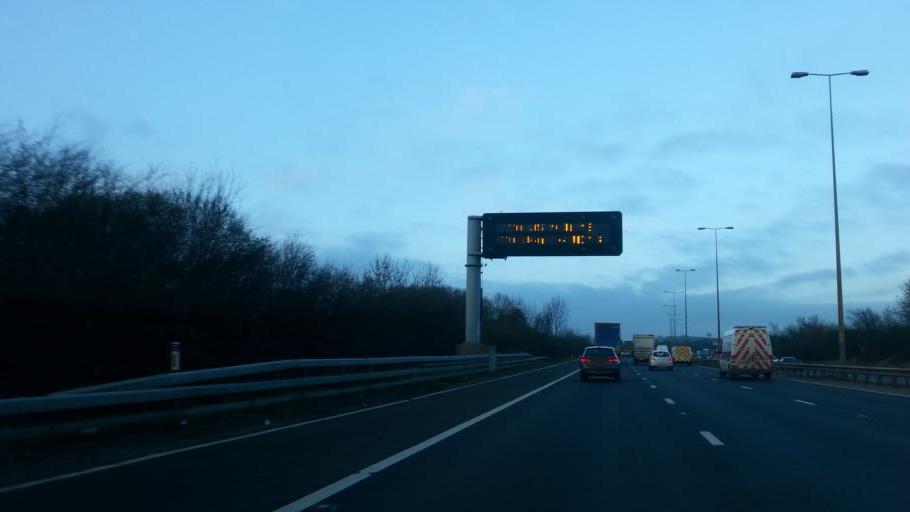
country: GB
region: England
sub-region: Worcestershire
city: Kempsey
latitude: 52.1542
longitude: -2.1909
